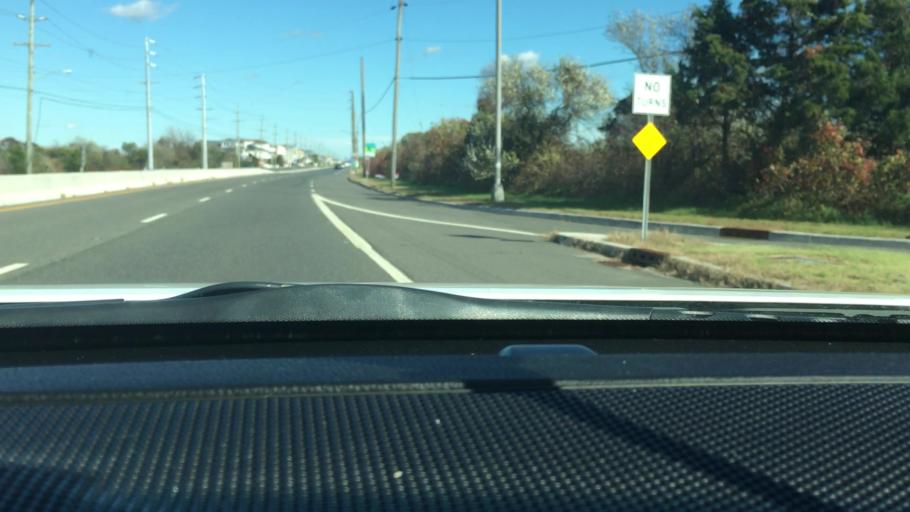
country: US
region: New Jersey
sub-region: Atlantic County
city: Atlantic City
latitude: 39.3880
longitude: -74.4170
